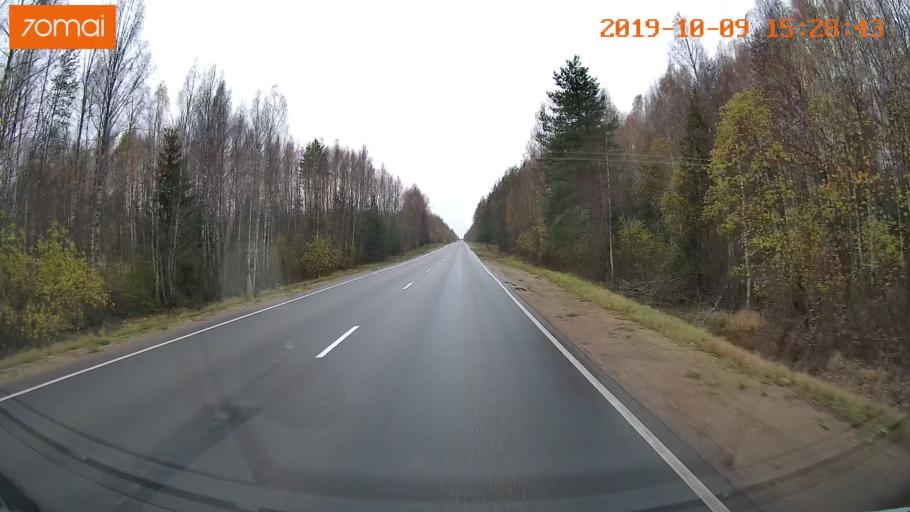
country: RU
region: Kostroma
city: Susanino
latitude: 57.9999
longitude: 41.3553
